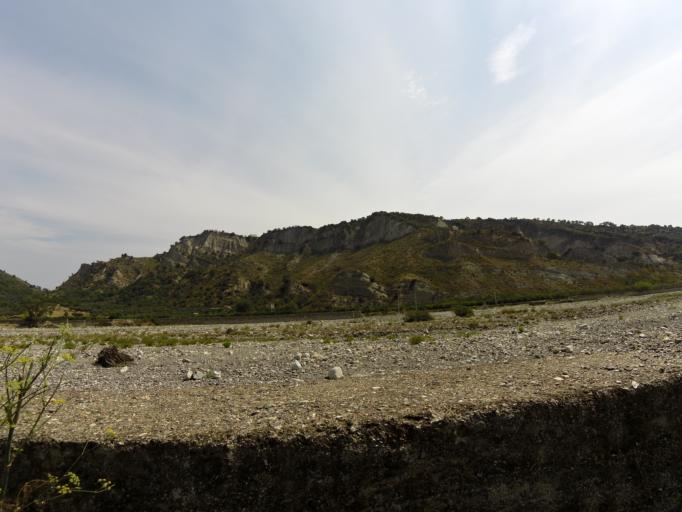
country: IT
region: Calabria
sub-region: Provincia di Reggio Calabria
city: Stilo
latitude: 38.4783
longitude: 16.4813
